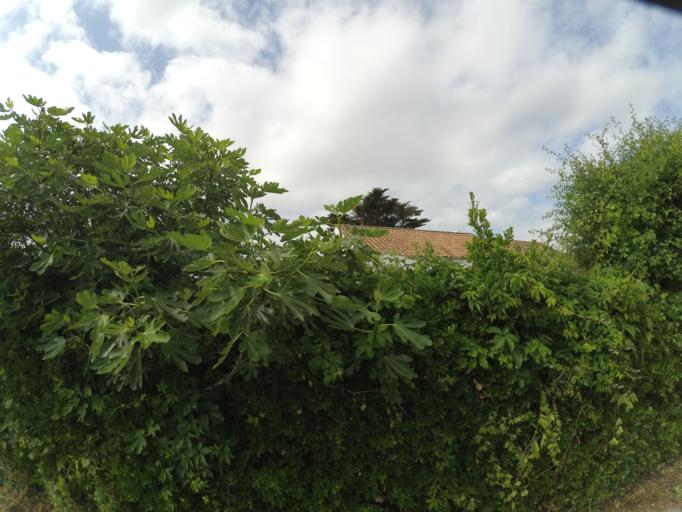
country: FR
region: Poitou-Charentes
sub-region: Departement de la Charente-Maritime
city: Angoulins
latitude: 46.0977
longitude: -1.1053
